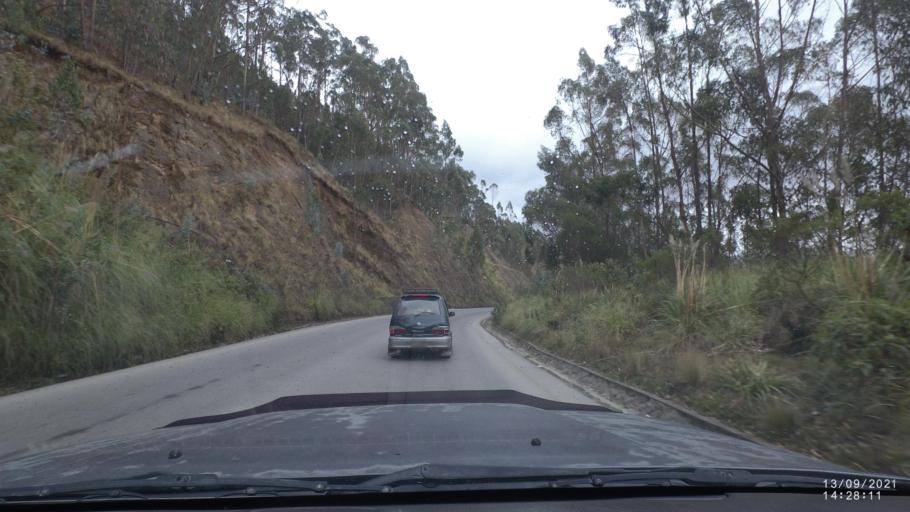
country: BO
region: Cochabamba
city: Colomi
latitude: -17.3172
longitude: -65.8639
